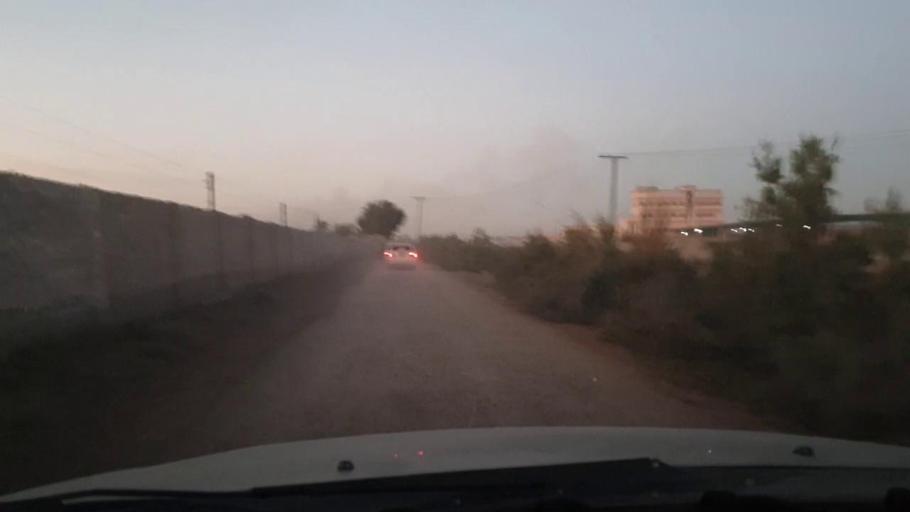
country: PK
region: Sindh
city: Ghotki
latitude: 27.9829
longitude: 69.2870
